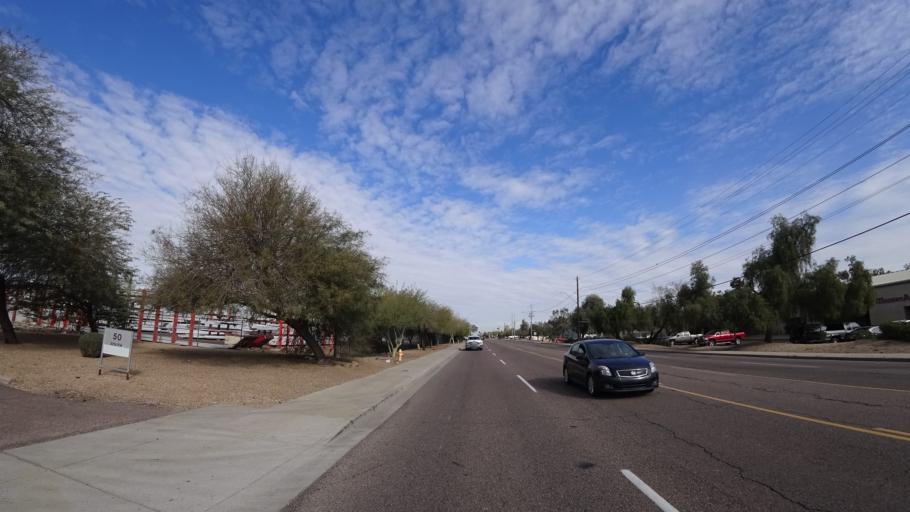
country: US
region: Arizona
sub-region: Maricopa County
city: Phoenix
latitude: 33.4483
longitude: -112.1519
